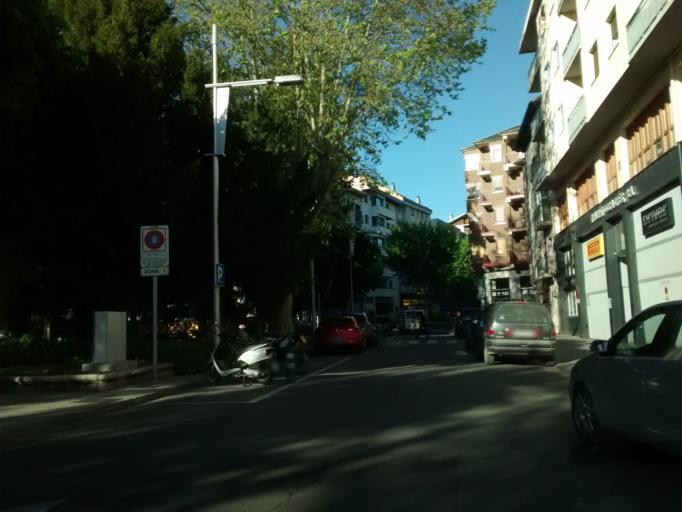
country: ES
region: Aragon
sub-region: Provincia de Huesca
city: Jaca
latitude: 42.5713
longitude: -0.5504
